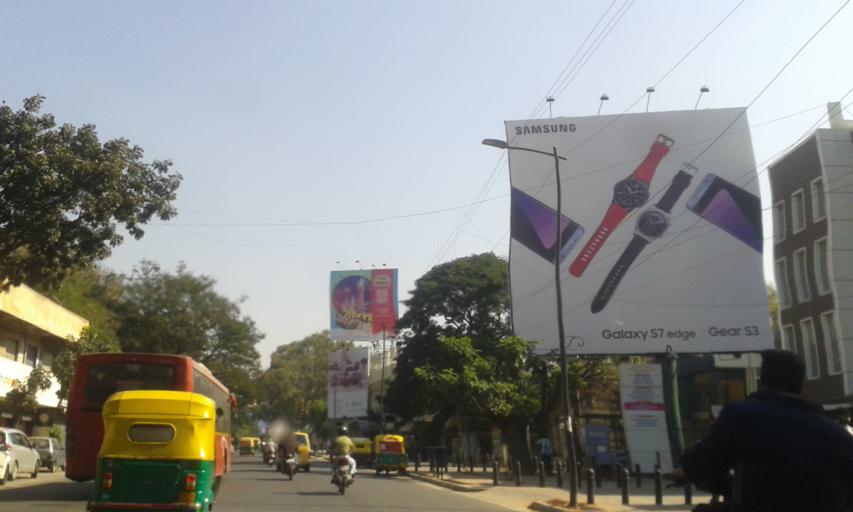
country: IN
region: Karnataka
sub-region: Bangalore Urban
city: Bangalore
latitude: 12.9687
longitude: 77.6015
